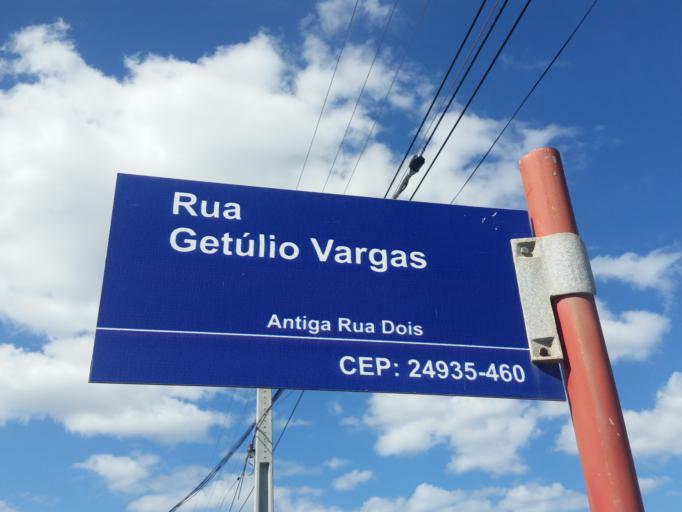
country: BR
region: Rio de Janeiro
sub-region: Marica
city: Marica
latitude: -22.9680
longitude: -42.9630
